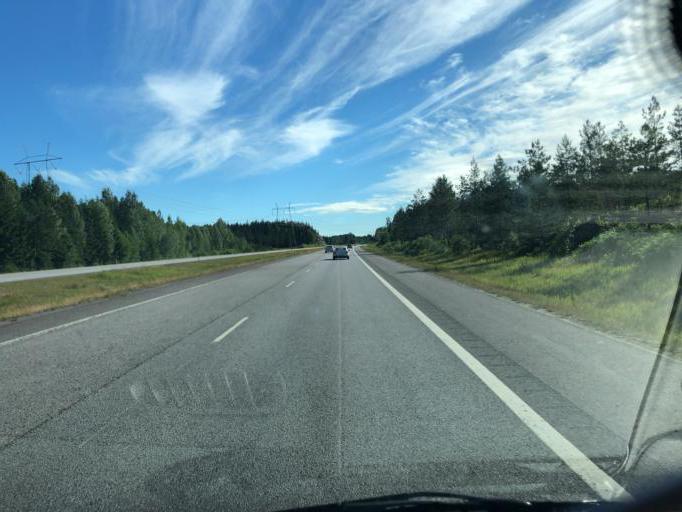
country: FI
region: Uusimaa
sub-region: Porvoo
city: Porvoo
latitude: 60.4456
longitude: 25.8314
